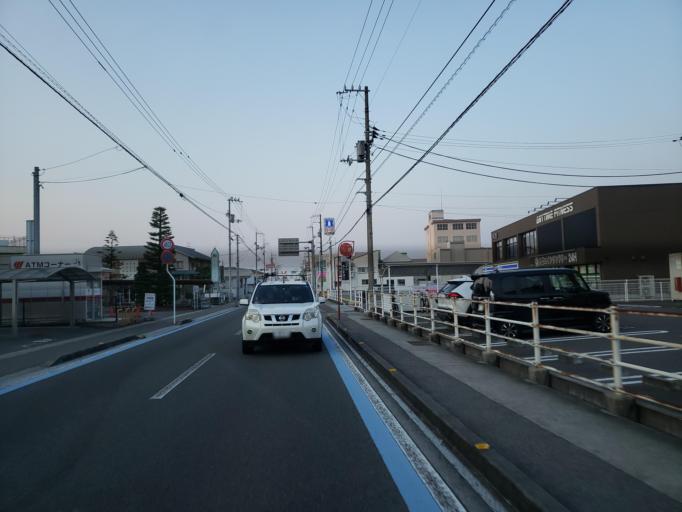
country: JP
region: Ehime
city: Hojo
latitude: 34.0418
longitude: 132.9763
